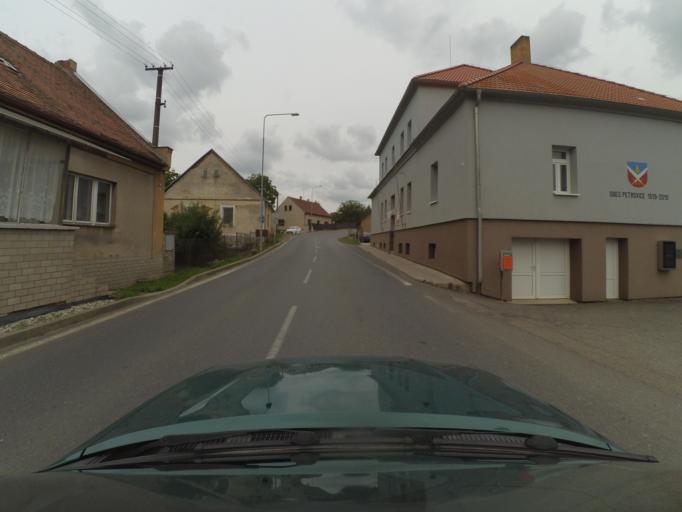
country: CZ
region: Central Bohemia
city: Pavlikov
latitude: 50.0672
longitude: 13.6390
